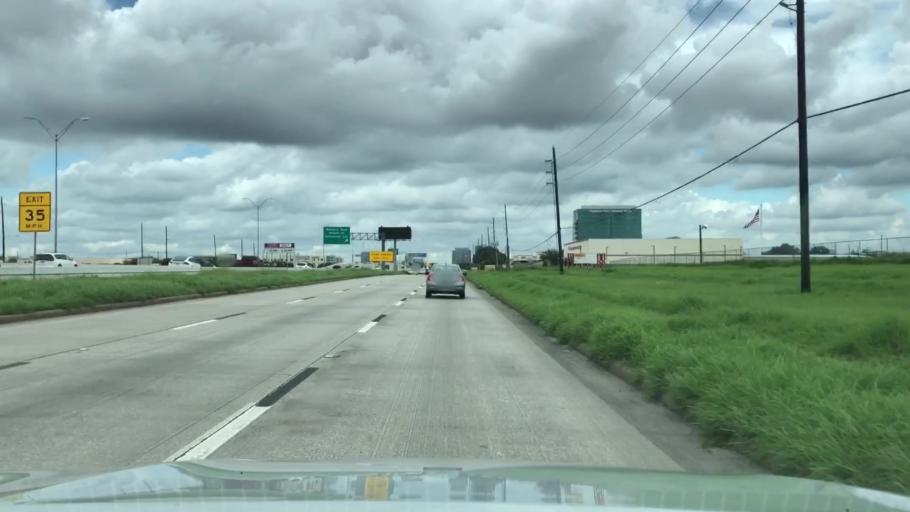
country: US
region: Texas
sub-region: Fort Bend County
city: Meadows Place
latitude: 29.6974
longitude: -95.5568
